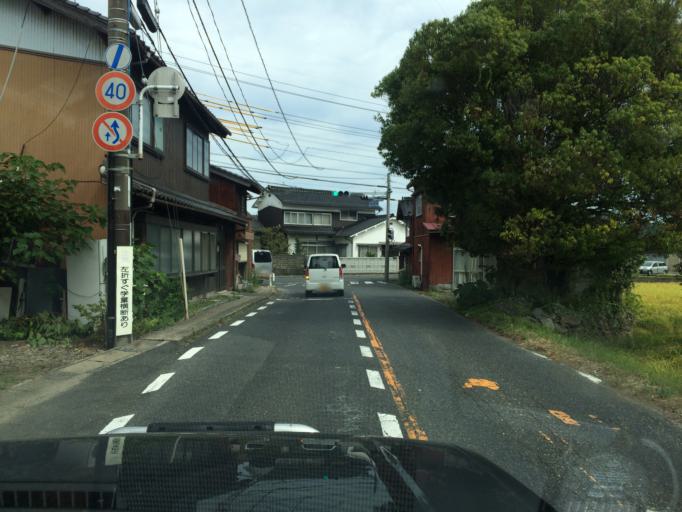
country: JP
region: Tottori
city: Tottori
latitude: 35.5008
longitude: 134.1983
